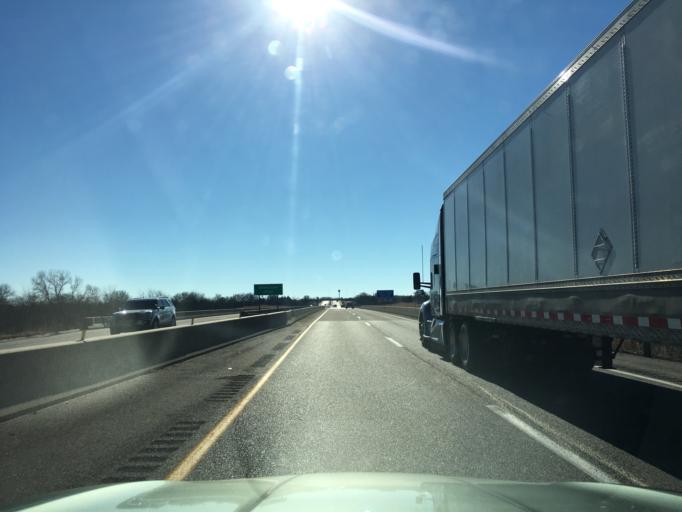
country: US
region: Kansas
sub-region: Sumner County
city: Belle Plaine
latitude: 37.3835
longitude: -97.3244
